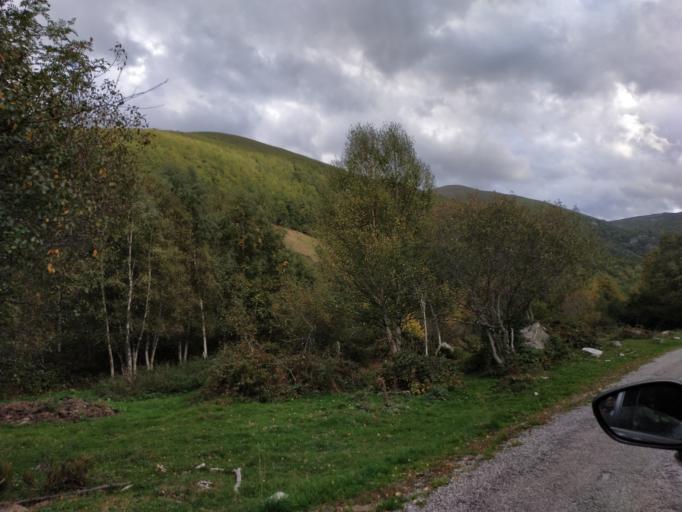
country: ES
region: Castille and Leon
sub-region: Provincia de Leon
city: Candin
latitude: 42.8612
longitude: -6.8561
